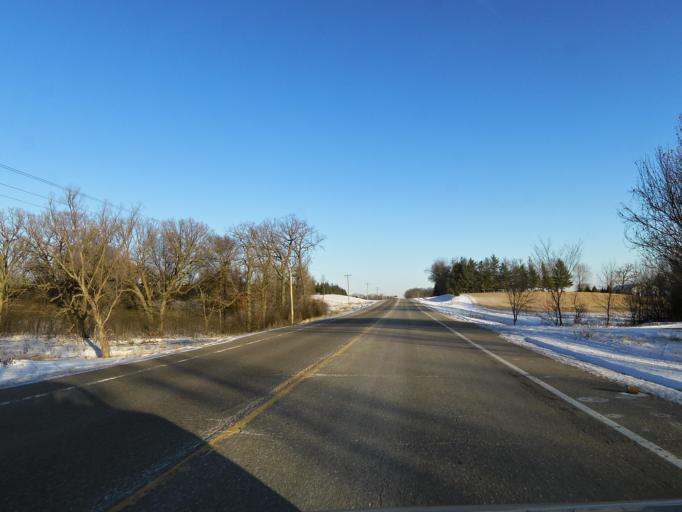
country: US
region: Minnesota
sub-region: Scott County
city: Elko New Market
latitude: 44.5439
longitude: -93.2758
